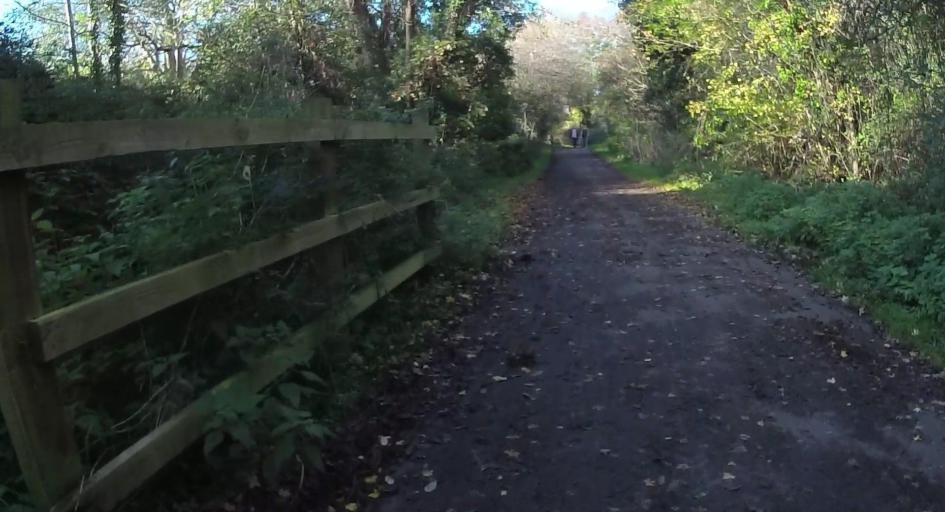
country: GB
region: England
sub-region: Wokingham
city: Wokingham
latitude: 51.4107
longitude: -0.8546
